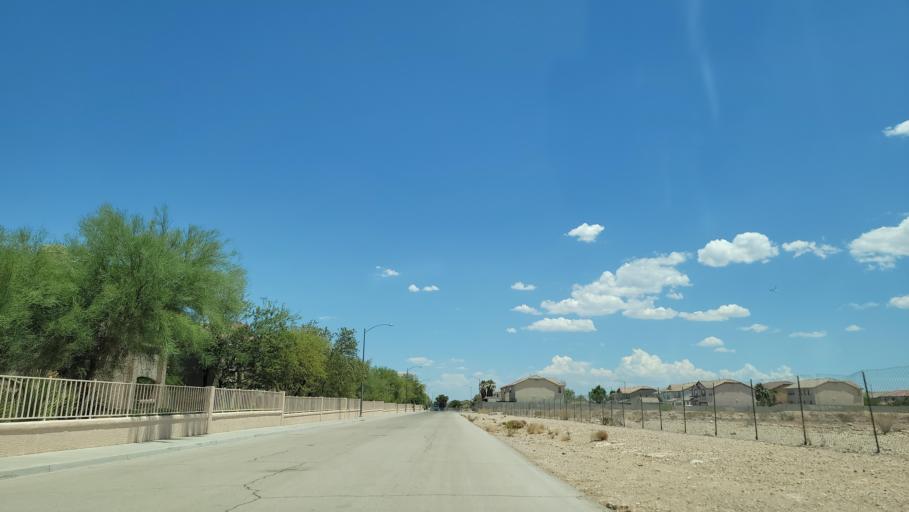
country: US
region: Nevada
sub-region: Clark County
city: Spring Valley
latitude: 36.0832
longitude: -115.2687
